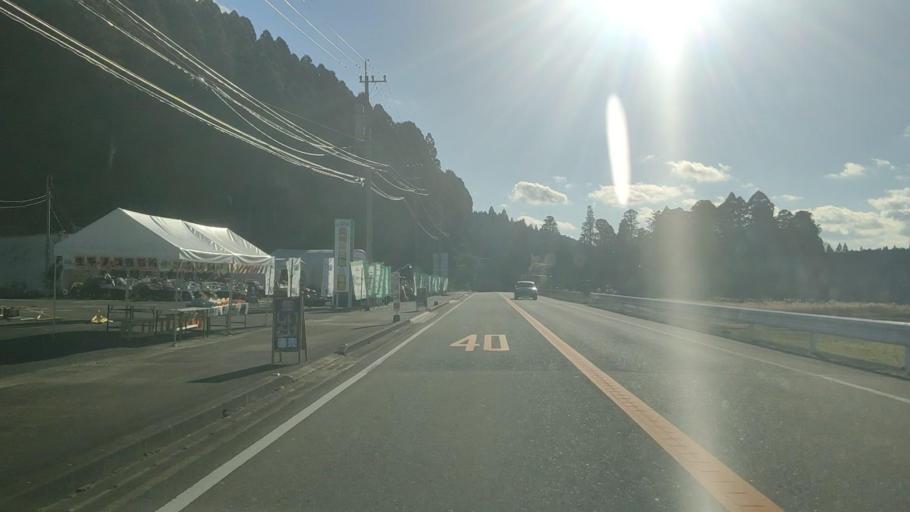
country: JP
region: Fukuoka
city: Maebaru-chuo
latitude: 33.4468
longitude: 130.2719
